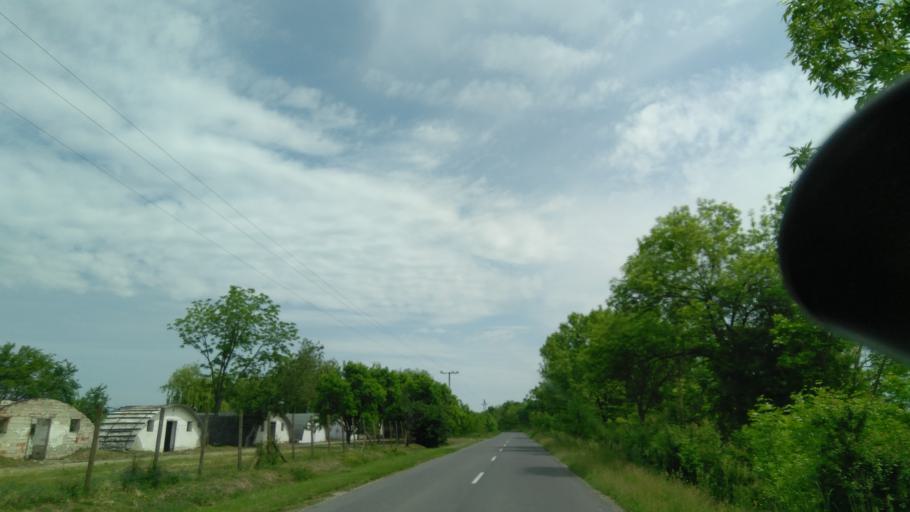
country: HU
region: Bekes
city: Fuzesgyarmat
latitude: 47.0991
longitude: 21.2371
